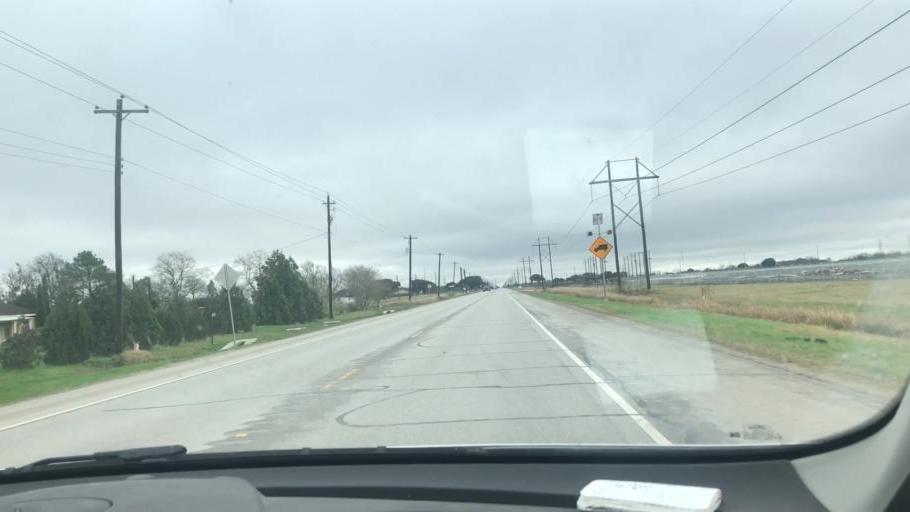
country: US
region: Texas
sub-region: Wharton County
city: Boling
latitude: 29.2085
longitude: -96.0252
